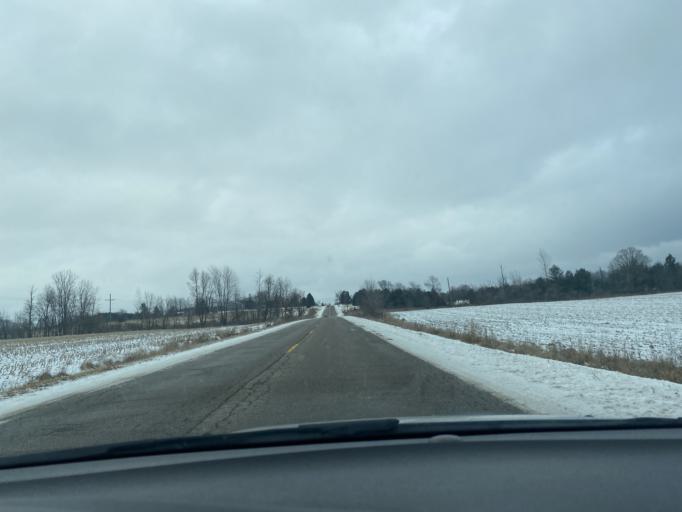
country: US
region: Michigan
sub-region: Lapeer County
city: North Branch
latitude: 43.2084
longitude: -83.1676
